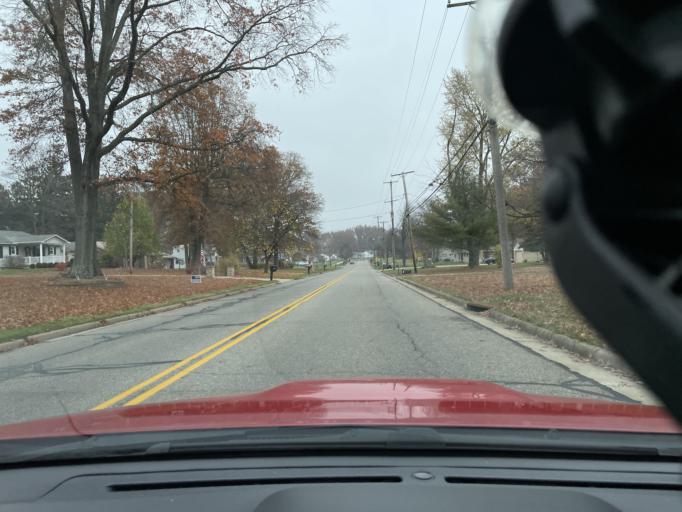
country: US
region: Ohio
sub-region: Mahoning County
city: Austintown
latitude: 41.1058
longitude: -80.7490
